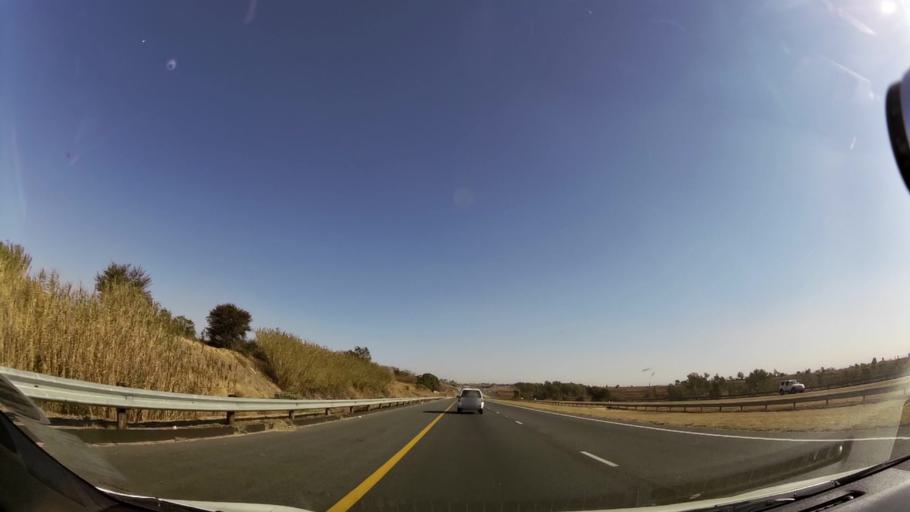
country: ZA
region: Gauteng
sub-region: City of Johannesburg Metropolitan Municipality
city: Diepsloot
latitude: -25.9769
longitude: 27.9354
